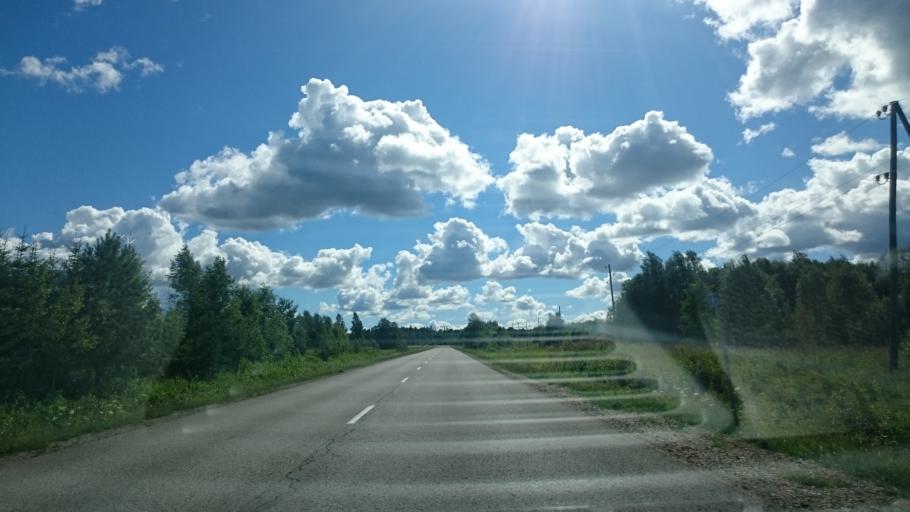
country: LV
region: Kuldigas Rajons
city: Kuldiga
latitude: 56.9052
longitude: 21.8990
